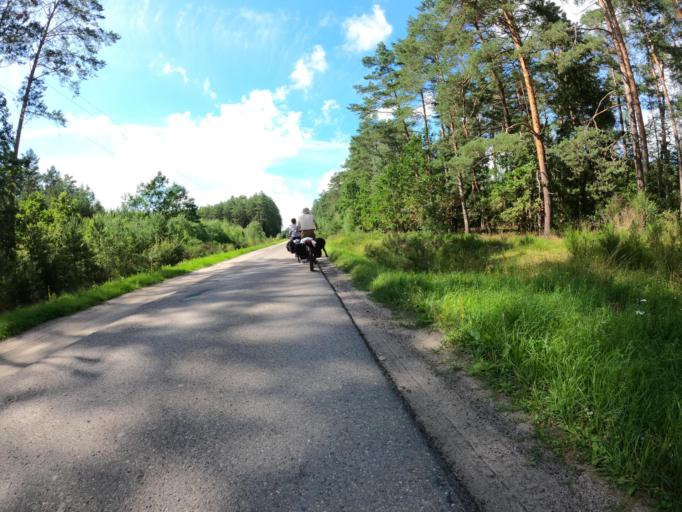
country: PL
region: West Pomeranian Voivodeship
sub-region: Powiat bialogardzki
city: Tychowo
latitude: 54.0332
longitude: 16.3440
